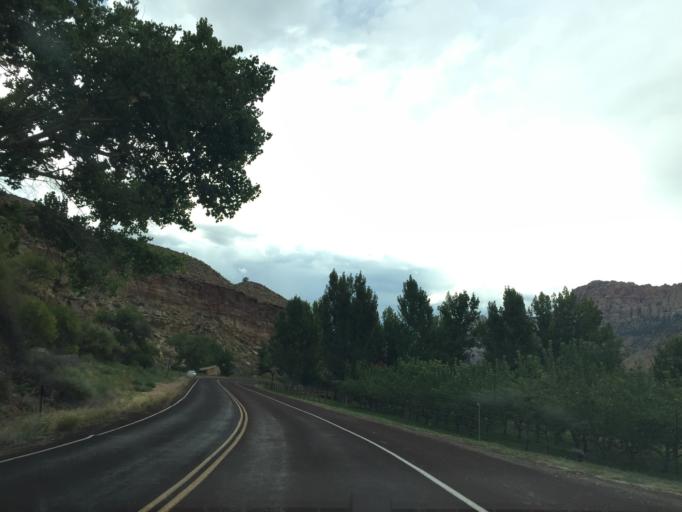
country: US
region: Utah
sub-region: Washington County
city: Hildale
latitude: 37.1613
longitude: -113.0181
